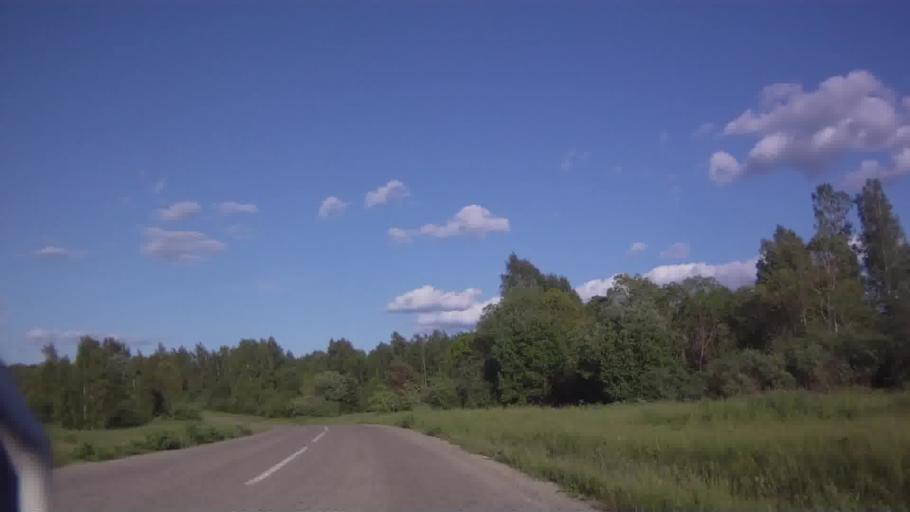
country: LV
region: Dagda
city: Dagda
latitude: 56.2810
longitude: 27.4798
